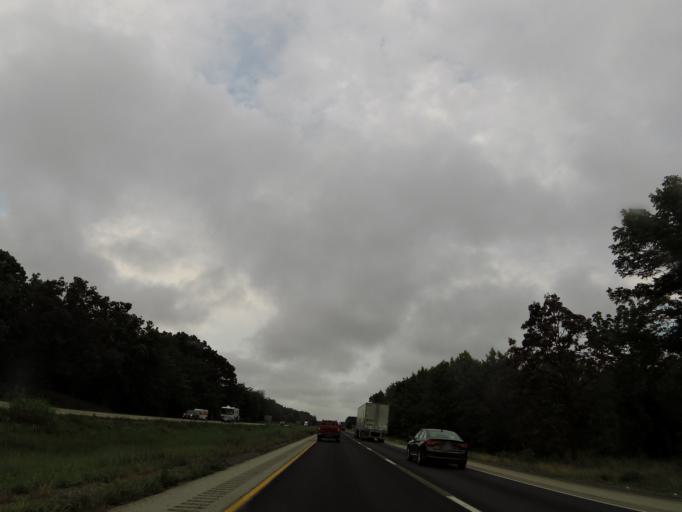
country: US
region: Illinois
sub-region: Franklin County
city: Benton
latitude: 38.0178
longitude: -88.9257
